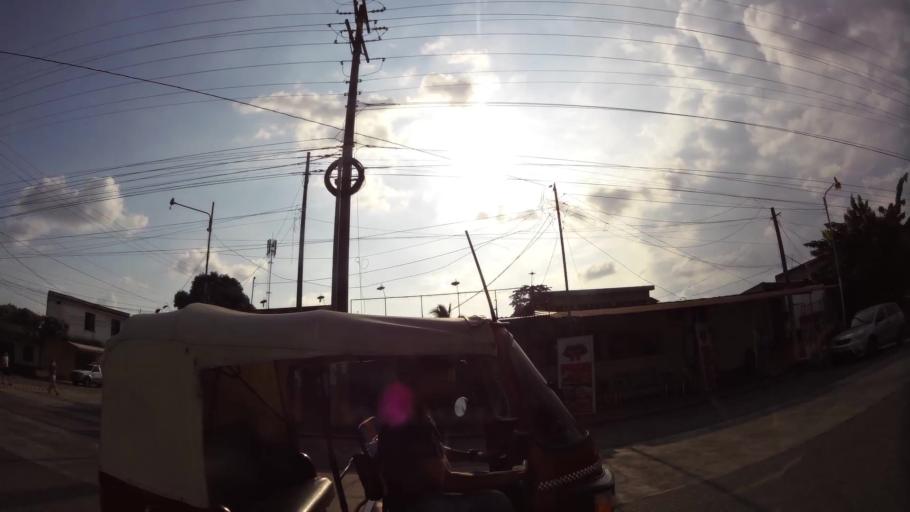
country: GT
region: Retalhuleu
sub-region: Municipio de Retalhuleu
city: Retalhuleu
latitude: 14.5403
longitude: -91.6756
